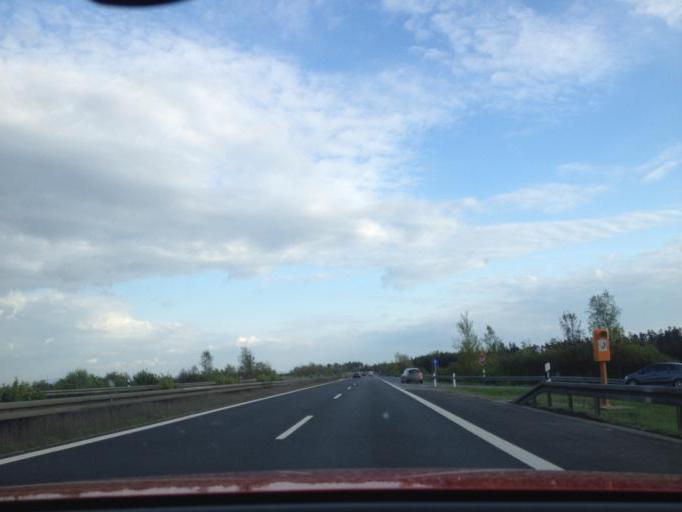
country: DE
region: Bavaria
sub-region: Upper Palatinate
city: Mitterteich
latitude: 49.9371
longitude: 12.2246
